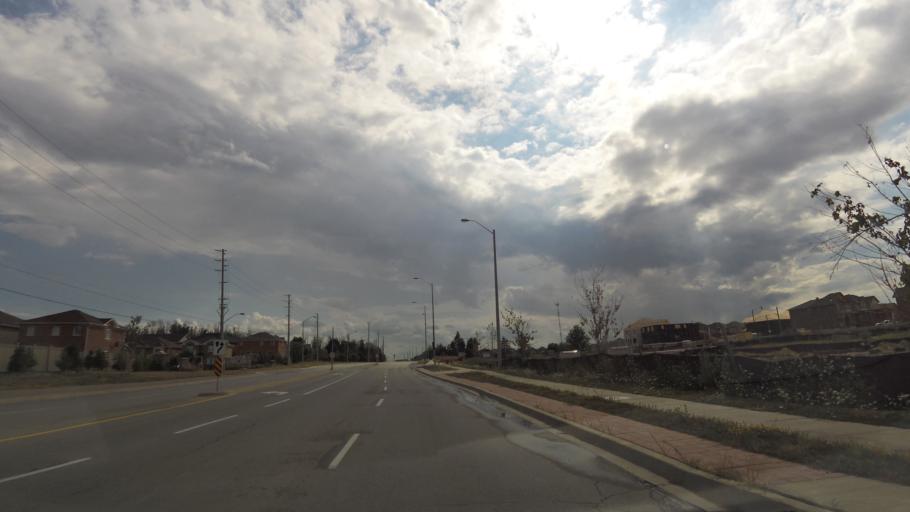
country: CA
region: Ontario
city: Brampton
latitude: 43.7028
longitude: -79.8389
